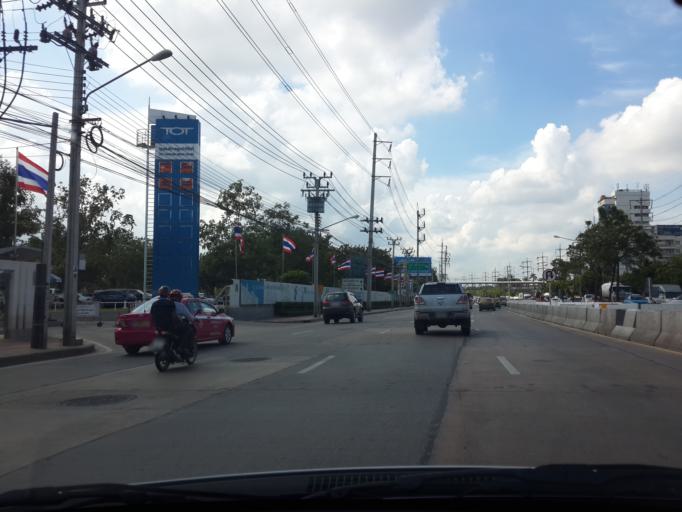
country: TH
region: Bangkok
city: Lak Si
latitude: 13.8868
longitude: 100.5767
